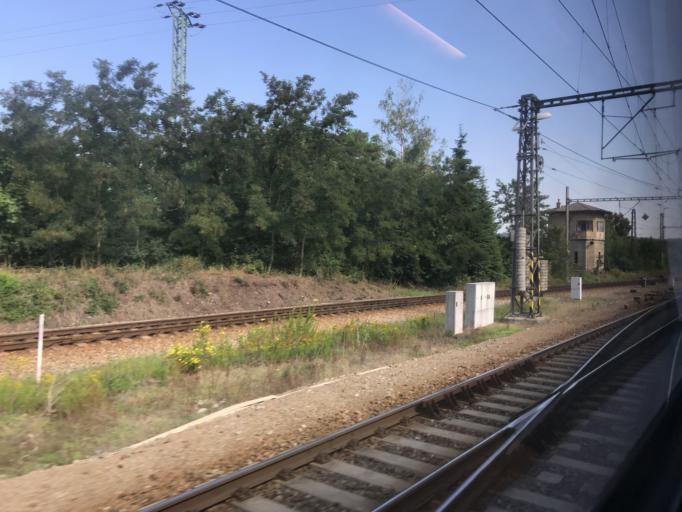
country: CZ
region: Central Bohemia
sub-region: Okres Benesov
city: Cercany
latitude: 49.8463
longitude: 14.6993
